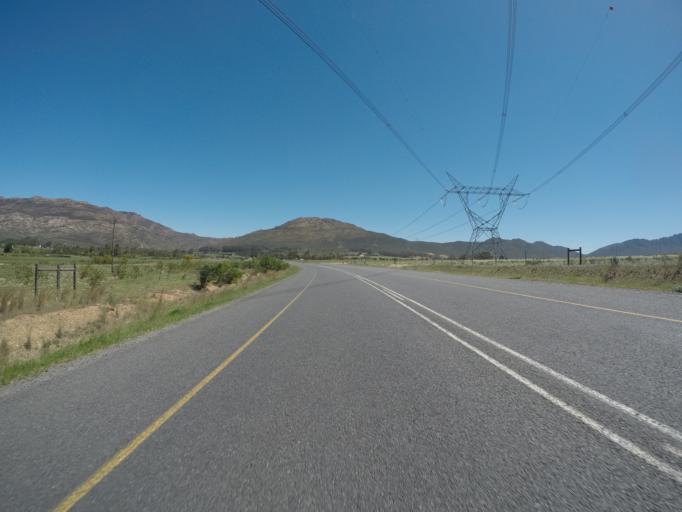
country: ZA
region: Western Cape
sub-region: Cape Winelands District Municipality
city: Ceres
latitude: -33.3081
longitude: 19.1111
